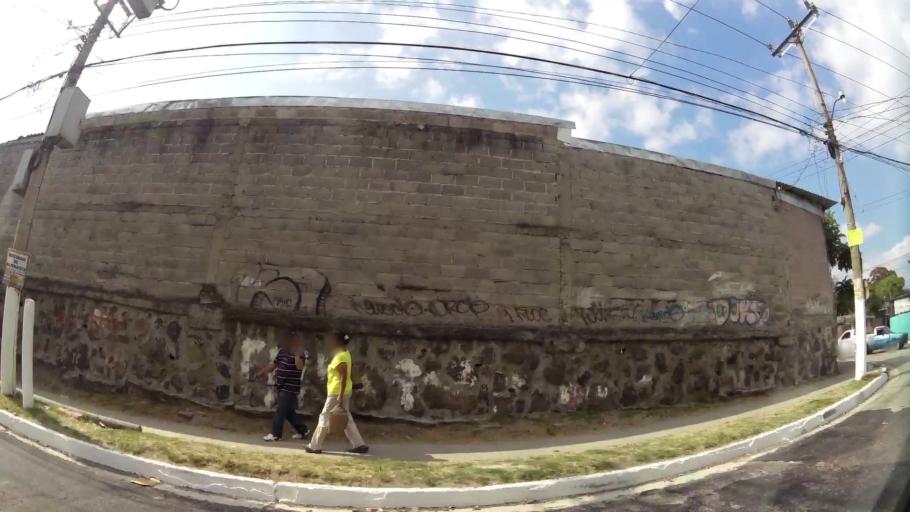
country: SV
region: San Salvador
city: Mejicanos
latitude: 13.7336
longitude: -89.2082
